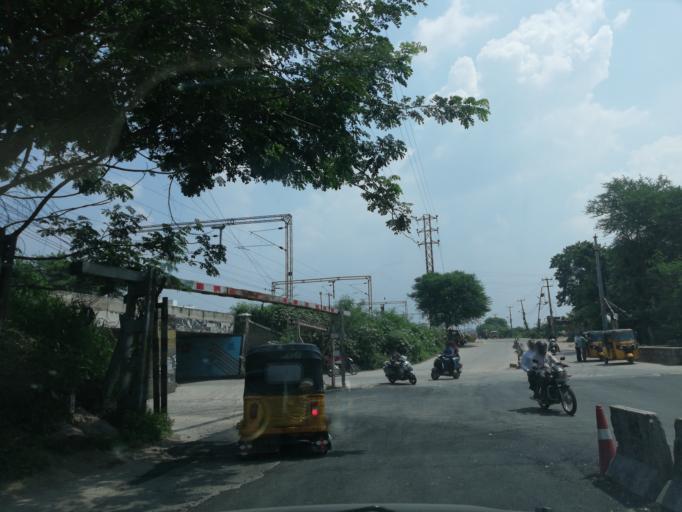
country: IN
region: Telangana
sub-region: Medak
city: Serilingampalle
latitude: 17.4845
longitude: 78.3208
